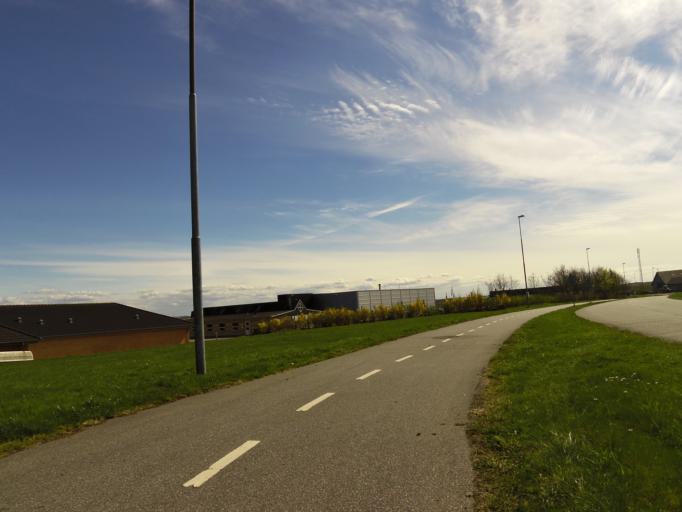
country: DK
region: Central Jutland
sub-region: Skive Kommune
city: Skive
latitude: 56.5716
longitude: 9.0004
